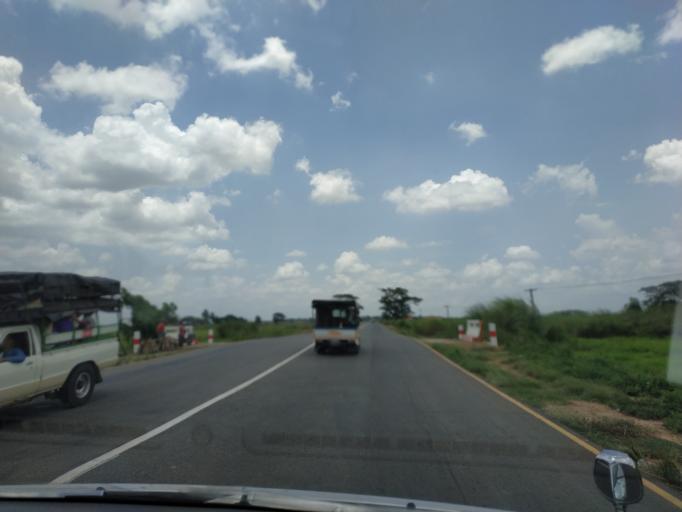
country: MM
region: Bago
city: Bago
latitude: 17.4691
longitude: 96.5657
